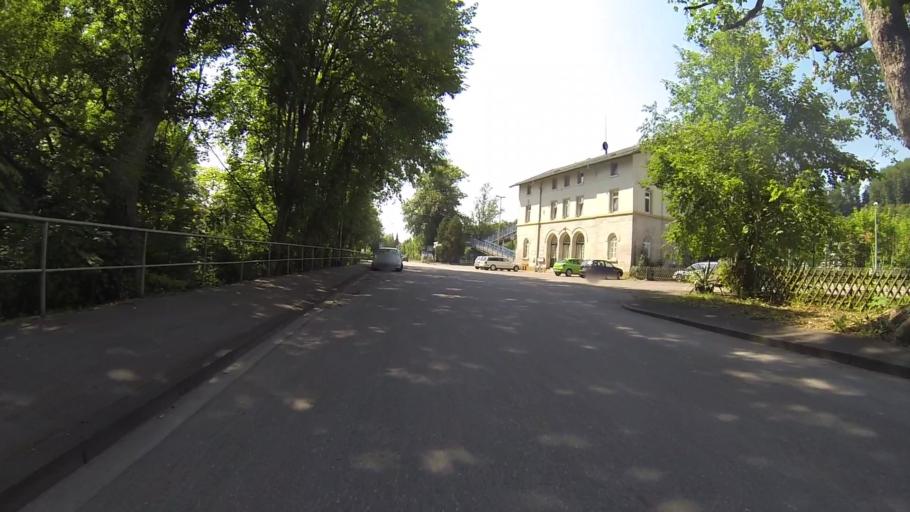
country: DE
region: Baden-Wuerttemberg
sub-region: Regierungsbezirk Stuttgart
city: Heidenheim an der Brenz
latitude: 48.7090
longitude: 10.1592
